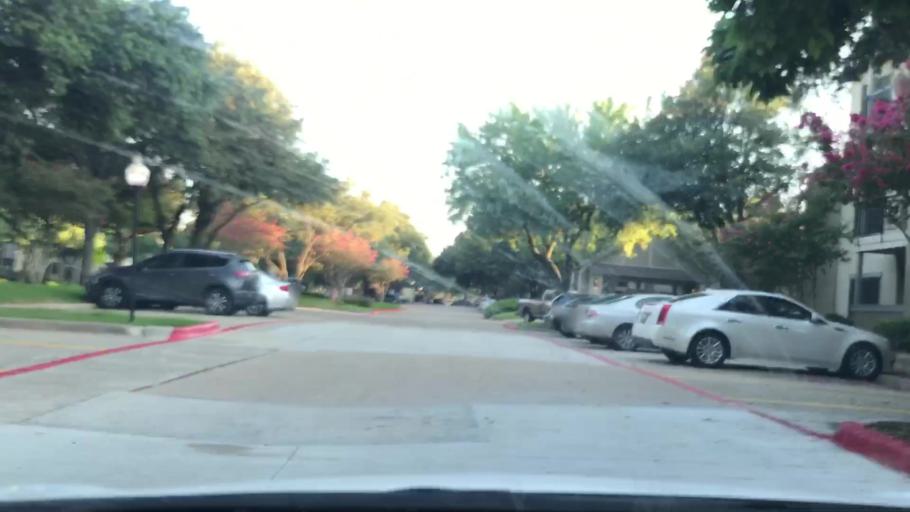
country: US
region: Texas
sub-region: Dallas County
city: Farmers Branch
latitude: 32.9282
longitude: -96.9486
